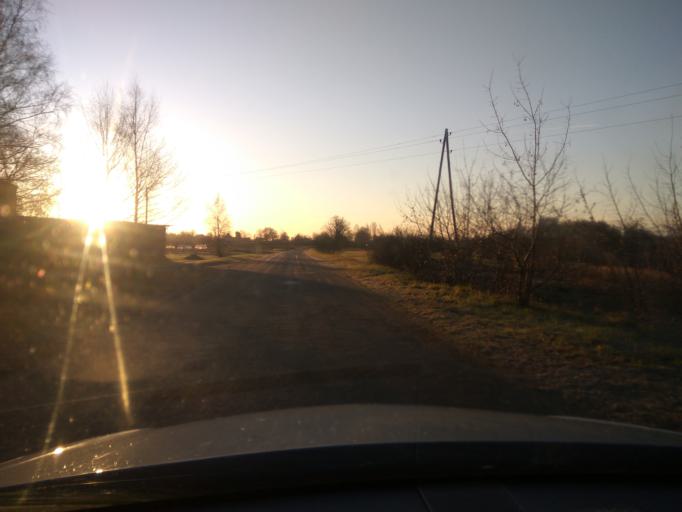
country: LV
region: Kuldigas Rajons
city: Kuldiga
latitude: 56.9655
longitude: 22.0039
